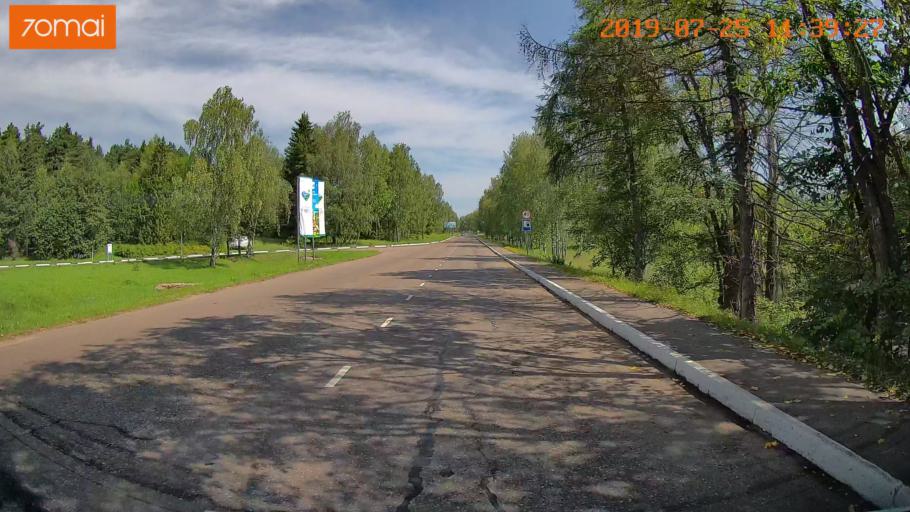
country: RU
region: Ivanovo
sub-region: Privolzhskiy Rayon
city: Ples
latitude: 57.4489
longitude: 41.4973
